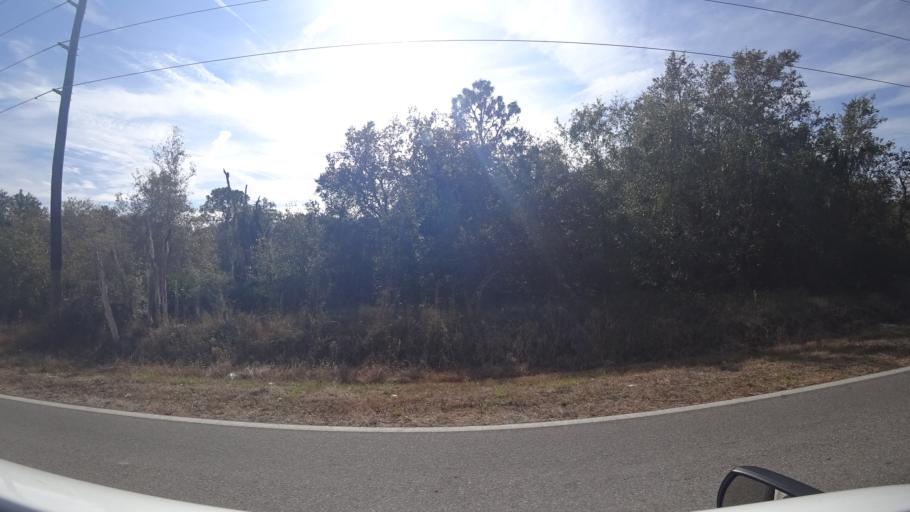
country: US
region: Florida
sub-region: Manatee County
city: Ellenton
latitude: 27.5853
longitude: -82.4359
